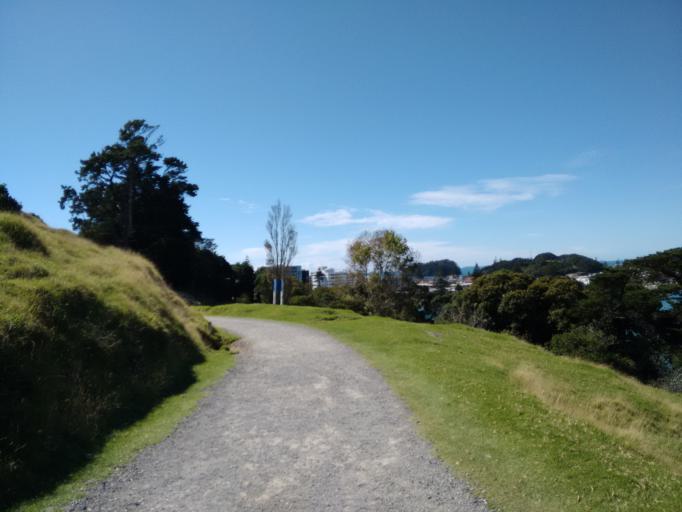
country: NZ
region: Bay of Plenty
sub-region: Tauranga City
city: Tauranga
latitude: -37.6351
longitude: 176.1720
